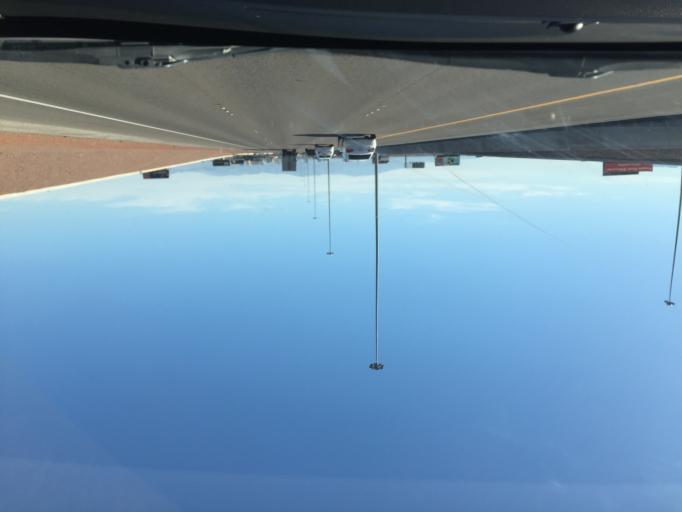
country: US
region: Nevada
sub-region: Clark County
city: Enterprise
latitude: 35.9624
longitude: -115.1816
